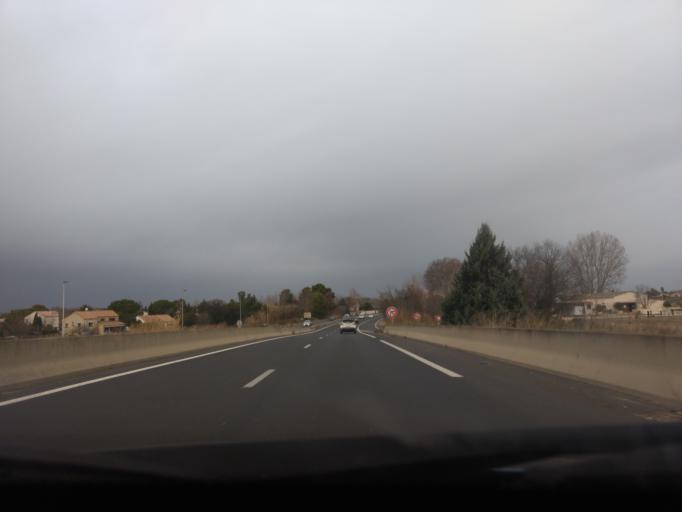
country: FR
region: Languedoc-Roussillon
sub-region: Departement de l'Herault
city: Lattes
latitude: 43.5553
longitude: 3.8930
